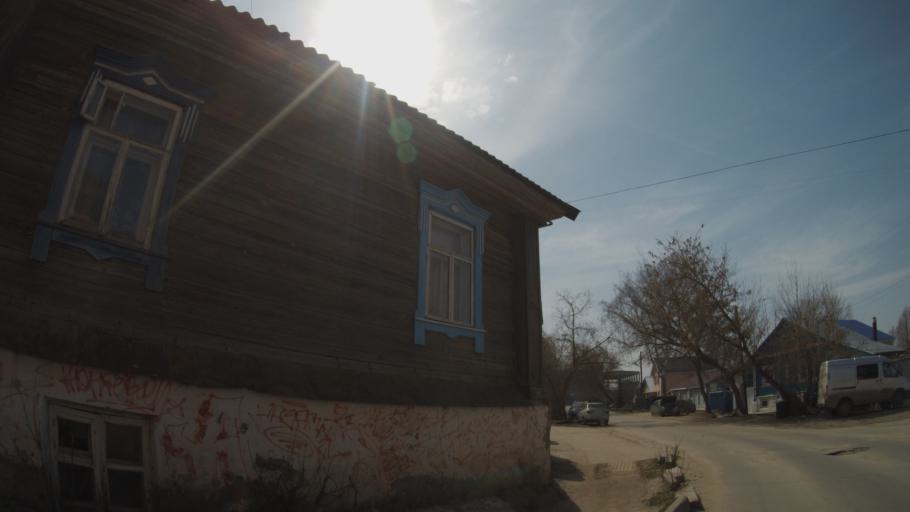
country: RU
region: Nizjnij Novgorod
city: Vyyezdnoye
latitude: 55.3855
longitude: 43.8117
